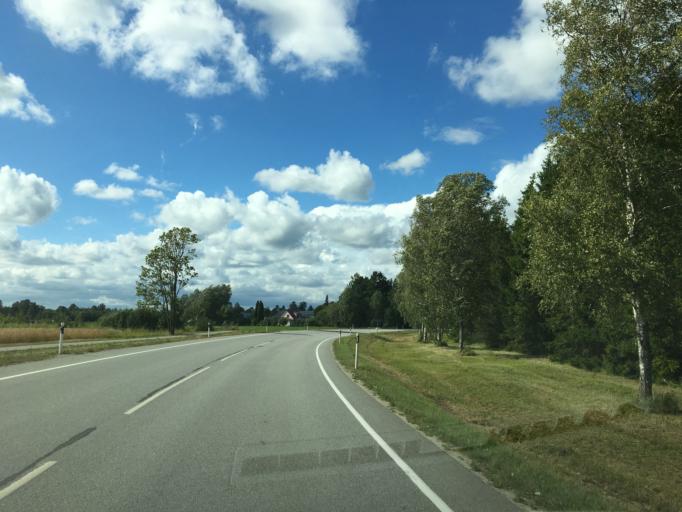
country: EE
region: Paernumaa
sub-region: Vaendra vald (alev)
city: Vandra
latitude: 58.6452
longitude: 25.0726
